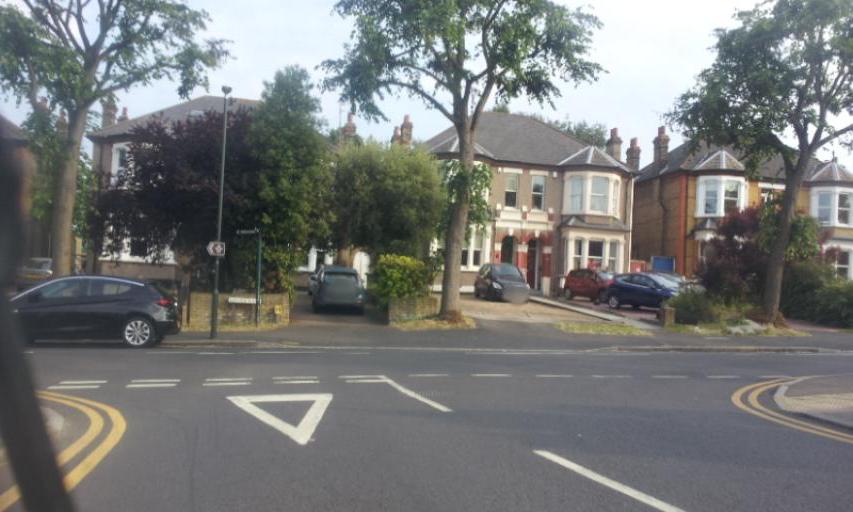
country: GB
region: England
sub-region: Greater London
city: Erith
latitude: 51.4775
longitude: 0.1766
